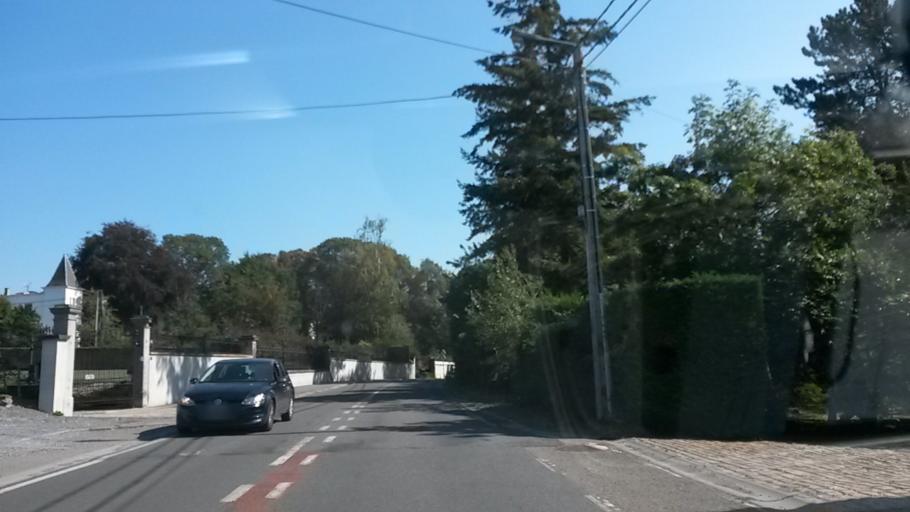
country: BE
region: Wallonia
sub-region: Province du Hainaut
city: Merbes-le-Chateau
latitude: 50.3228
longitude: 4.1532
